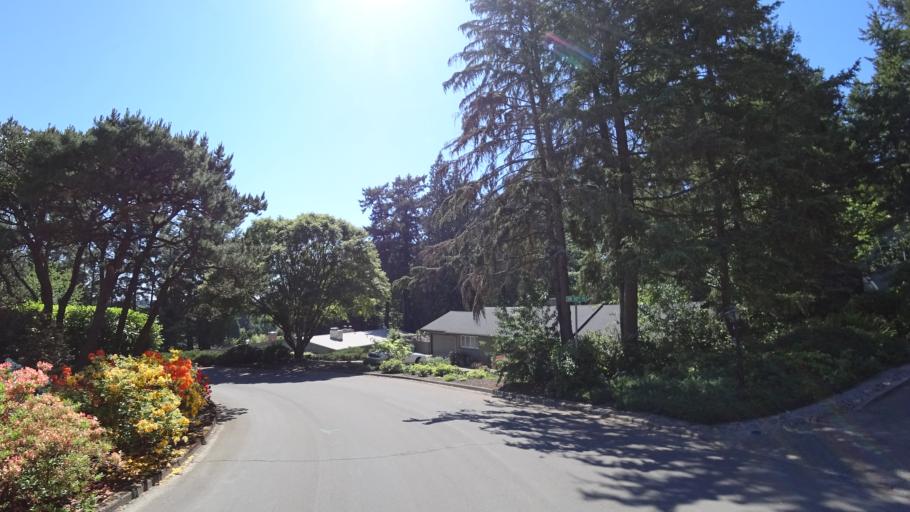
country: US
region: Oregon
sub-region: Washington County
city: West Slope
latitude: 45.4974
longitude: -122.7291
